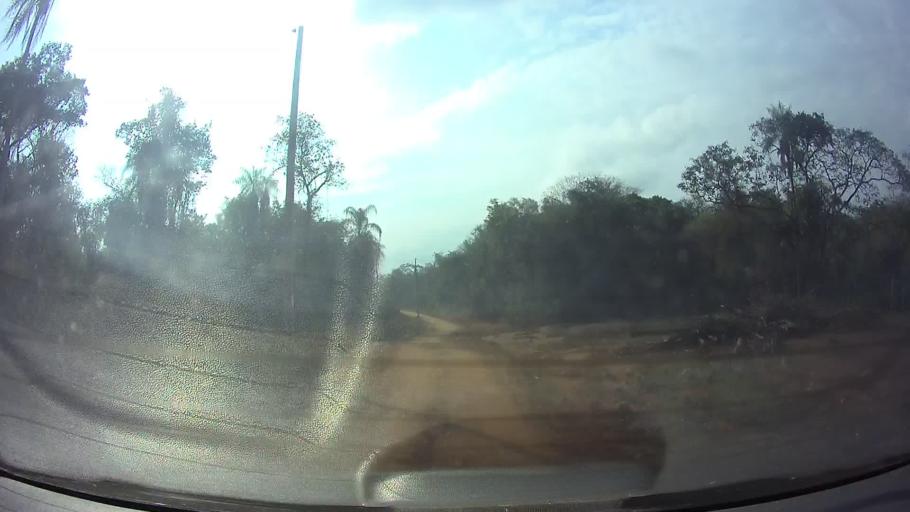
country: PY
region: Cordillera
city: Arroyos y Esteros
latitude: -25.0164
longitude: -57.1966
